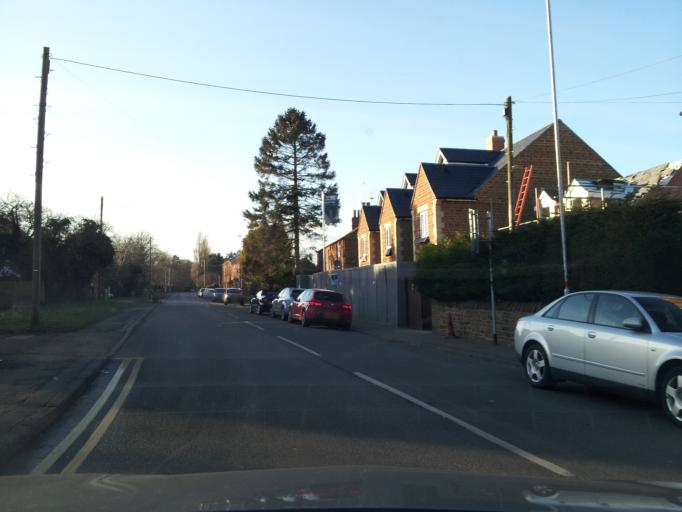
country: GB
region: England
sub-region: Northamptonshire
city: Northampton
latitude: 52.2591
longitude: -0.9532
